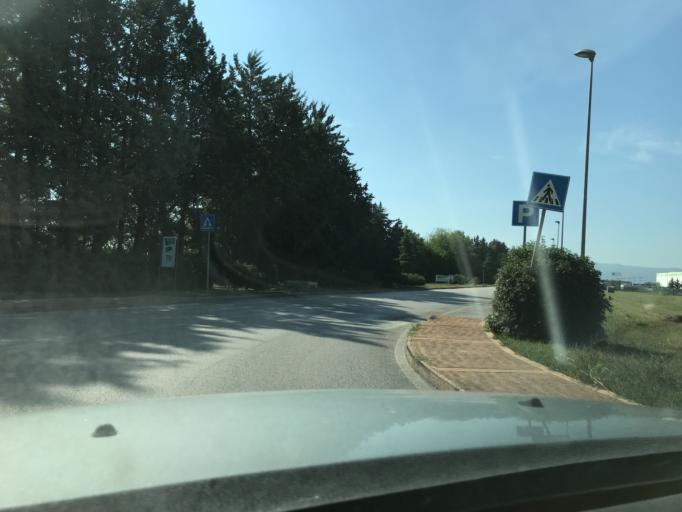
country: IT
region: Umbria
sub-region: Provincia di Perugia
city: Ospedalicchio
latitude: 43.0784
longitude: 12.5098
